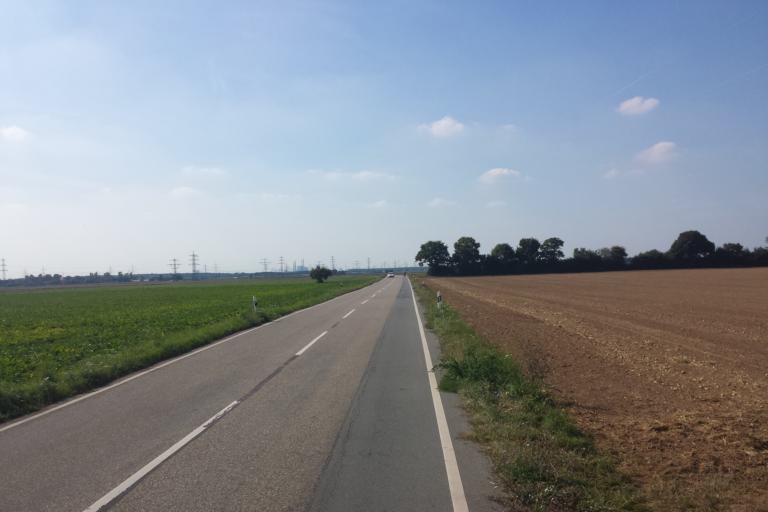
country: DE
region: Baden-Wuerttemberg
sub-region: Karlsruhe Region
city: Eppelheim
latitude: 49.4179
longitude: 8.6158
